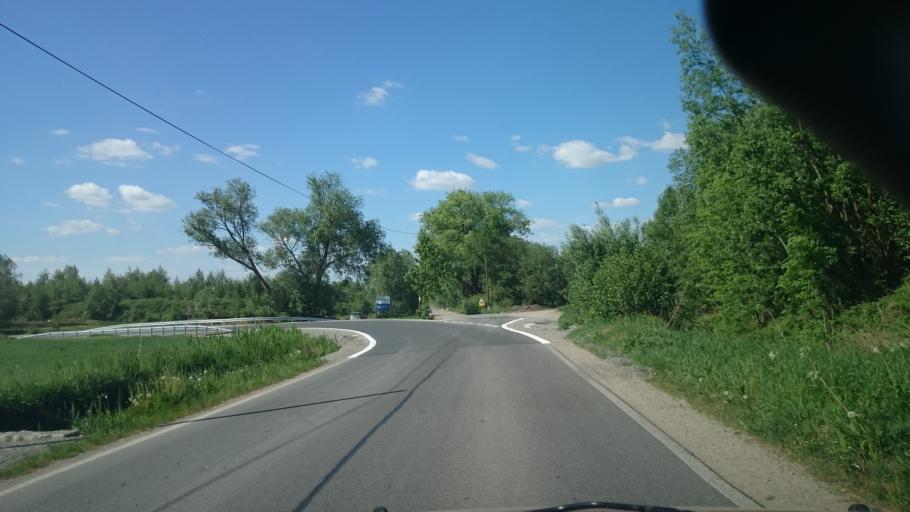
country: PL
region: Lower Silesian Voivodeship
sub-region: Powiat zabkowicki
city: Kamieniec Zabkowicki
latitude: 50.5063
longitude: 16.8322
